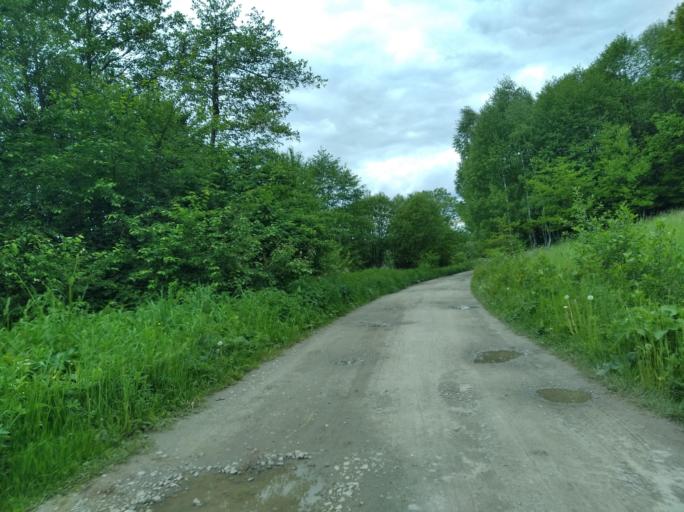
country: PL
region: Subcarpathian Voivodeship
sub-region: Powiat brzozowski
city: Jasionow
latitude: 49.6719
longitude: 21.9791
